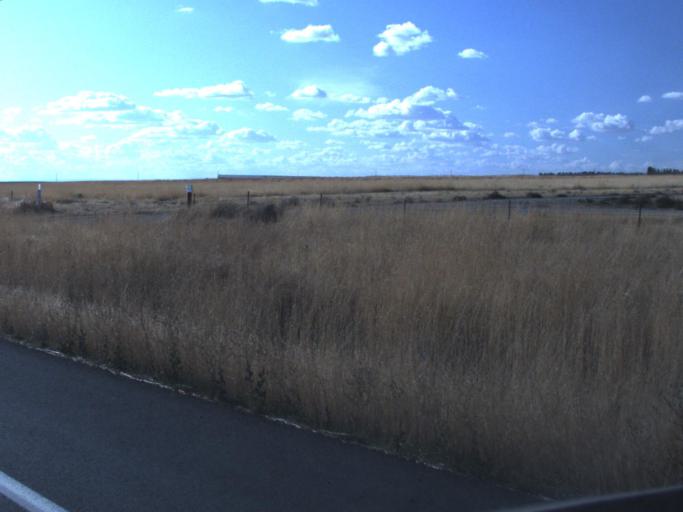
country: US
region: Oregon
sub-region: Umatilla County
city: Umatilla
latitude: 45.9571
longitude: -119.4146
